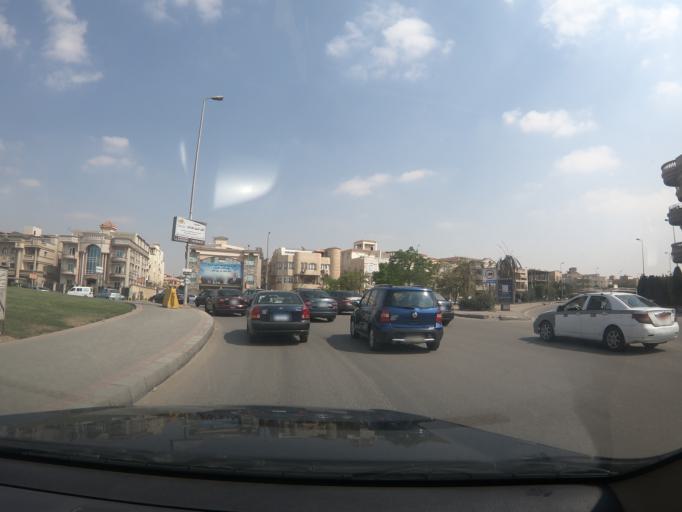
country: EG
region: Muhafazat al Qahirah
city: Cairo
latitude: 30.0159
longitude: 31.4452
